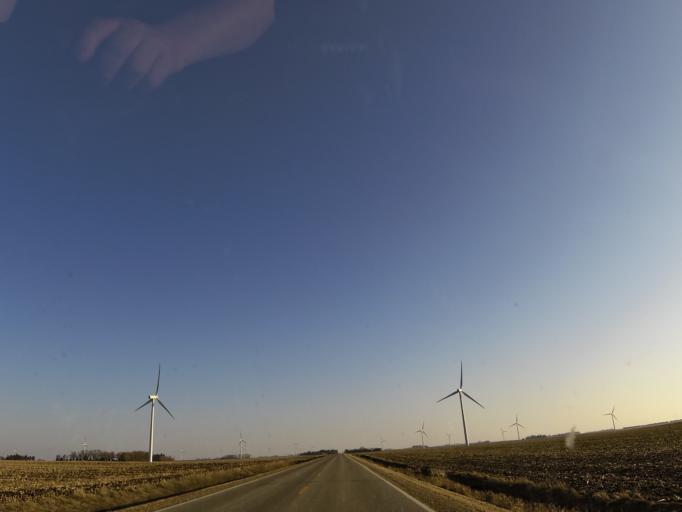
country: US
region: Iowa
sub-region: Worth County
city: Northwood
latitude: 43.4285
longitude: -93.1245
